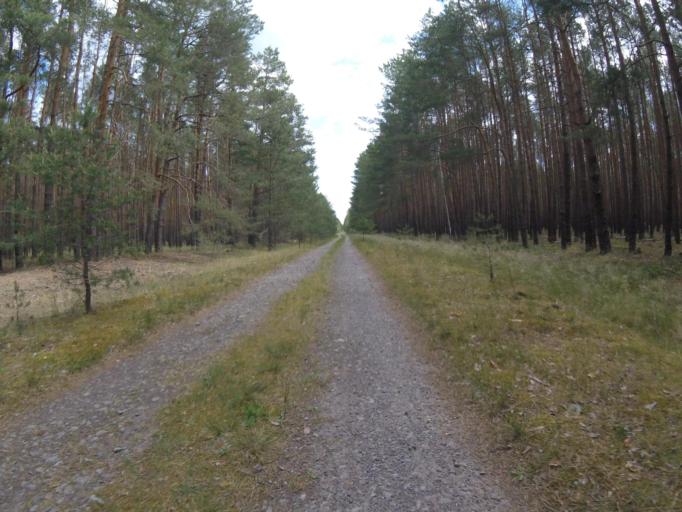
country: DE
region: Brandenburg
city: Halbe
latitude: 52.0975
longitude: 13.6606
